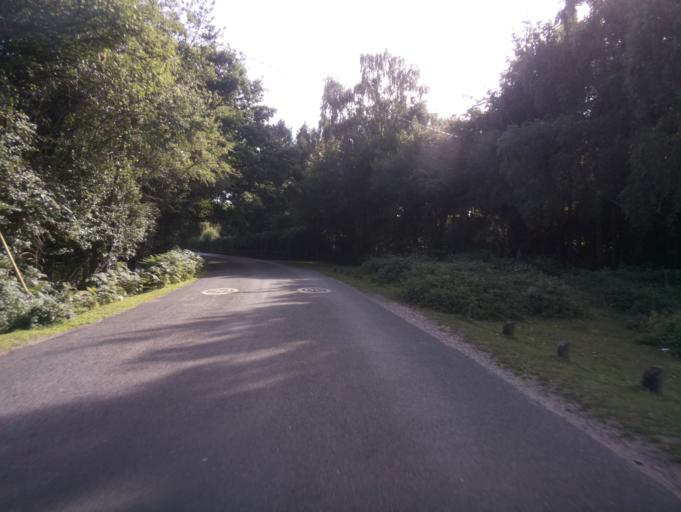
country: GB
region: England
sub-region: Hampshire
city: West Wellow
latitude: 50.9492
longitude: -1.5913
